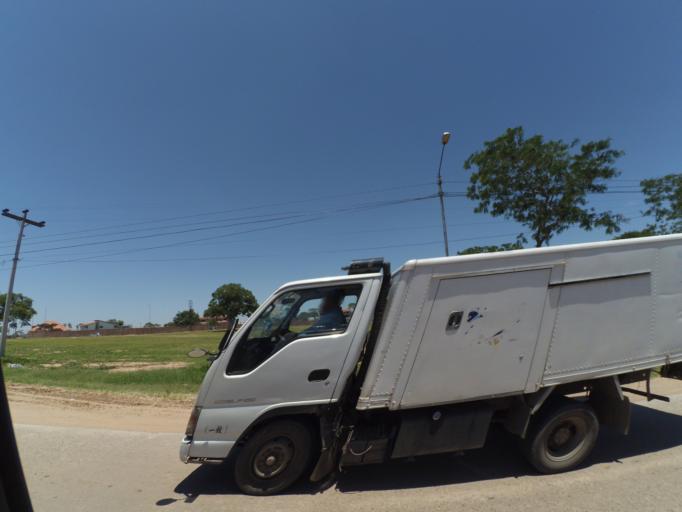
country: BO
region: Santa Cruz
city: Santa Cruz de la Sierra
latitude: -17.7542
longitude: -63.2186
